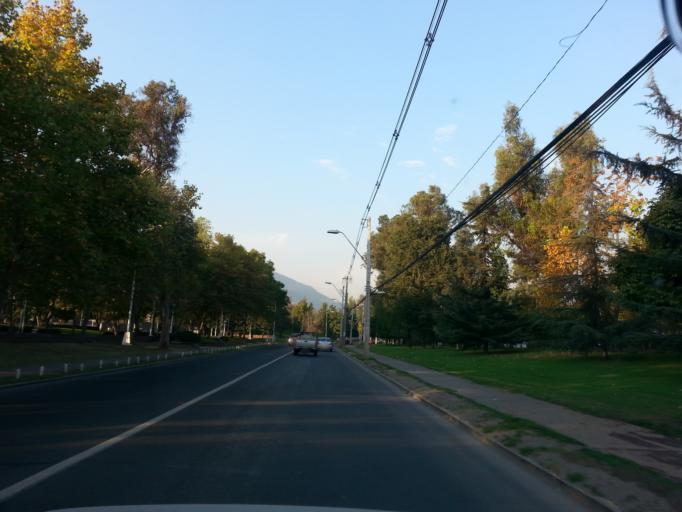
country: CL
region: Santiago Metropolitan
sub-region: Provincia de Santiago
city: Villa Presidente Frei, Nunoa, Santiago, Chile
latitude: -33.3849
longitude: -70.5898
